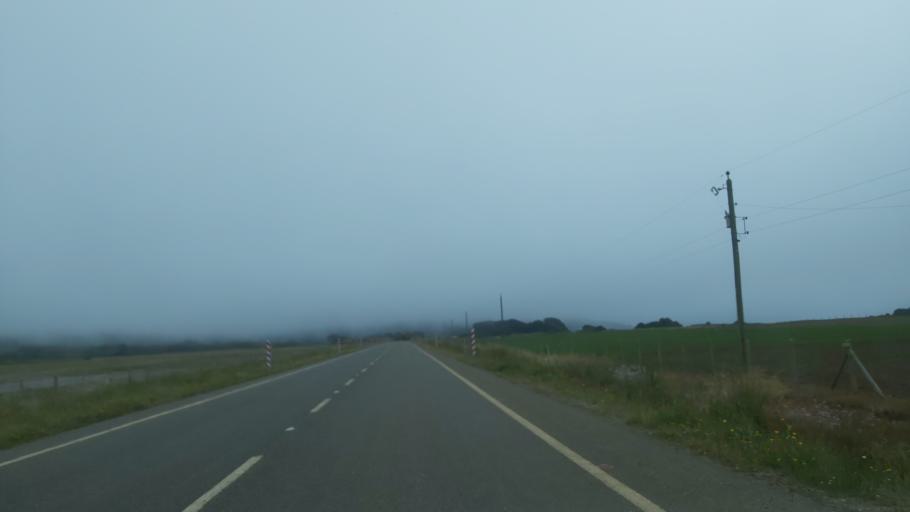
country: CL
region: Maule
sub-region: Provincia de Cauquenes
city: Cauquenes
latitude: -35.9968
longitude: -72.7712
